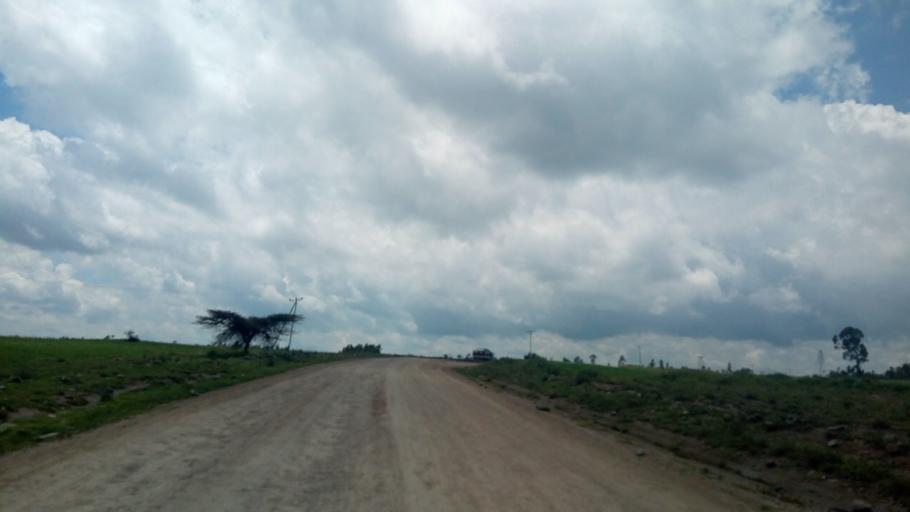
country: ET
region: Oromiya
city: Sendafa
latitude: 8.9888
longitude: 39.1246
